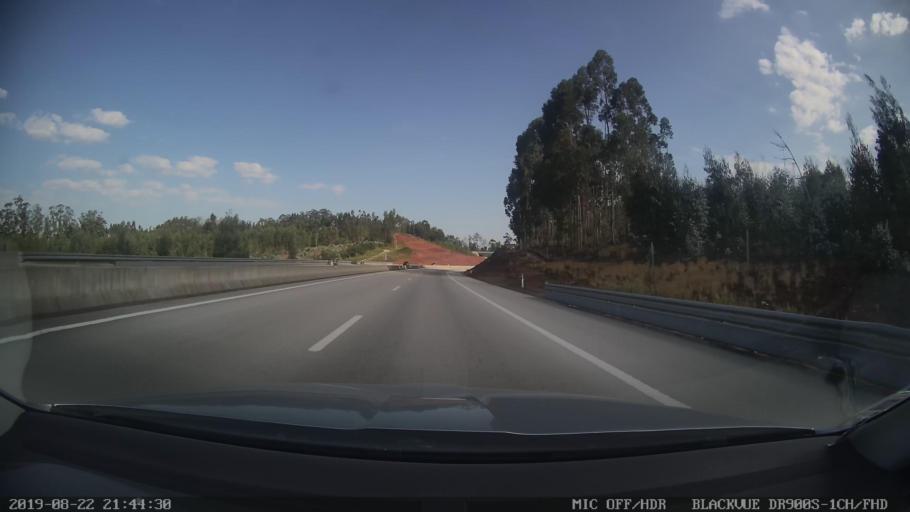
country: PT
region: Coimbra
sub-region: Penela
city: Penela
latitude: 39.9528
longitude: -8.3500
